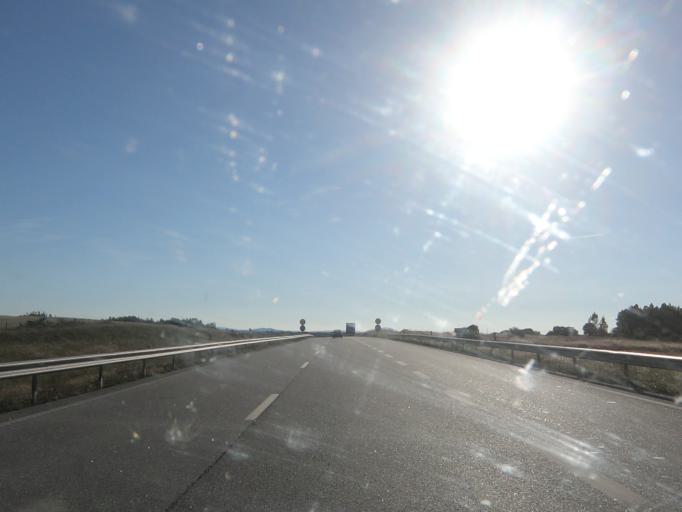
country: ES
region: Castille and Leon
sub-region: Provincia de Salamanca
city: Fuentes de Onoro
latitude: 40.6045
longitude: -6.9563
